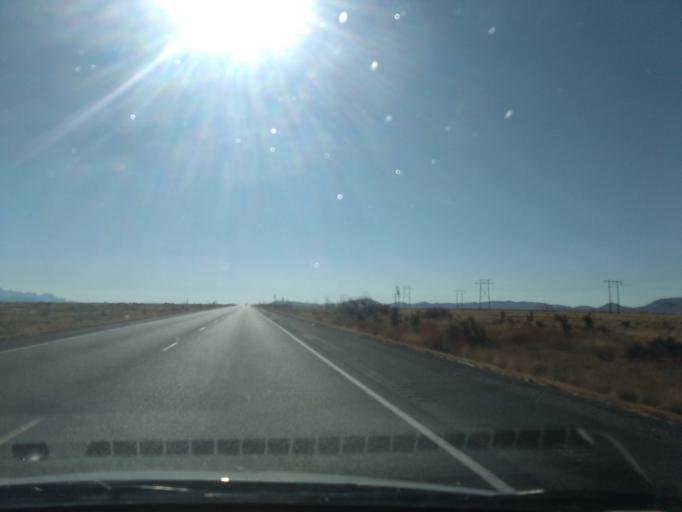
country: US
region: New Mexico
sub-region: Luna County
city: Deming
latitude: 32.4685
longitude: -107.5374
